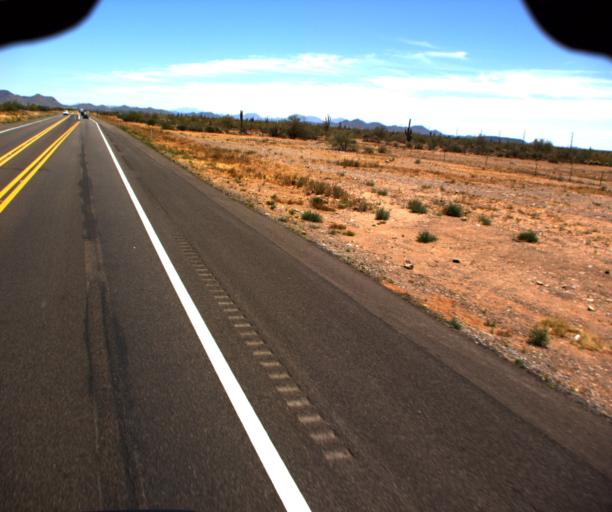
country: US
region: Arizona
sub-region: Maricopa County
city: Anthem
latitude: 33.7977
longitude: -112.2093
